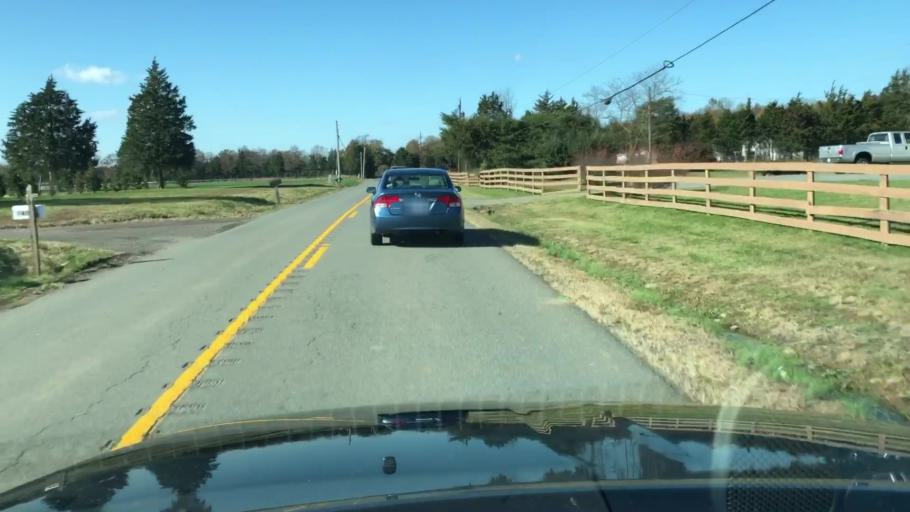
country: US
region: Virginia
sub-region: Fauquier County
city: Bealeton
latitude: 38.5209
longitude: -77.7965
